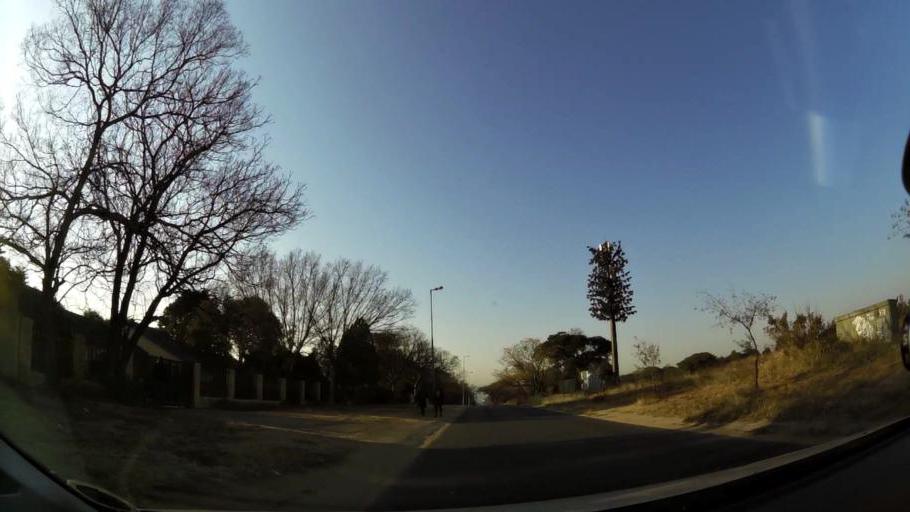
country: ZA
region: Gauteng
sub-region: City of Johannesburg Metropolitan Municipality
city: Modderfontein
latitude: -26.0783
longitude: 28.0980
